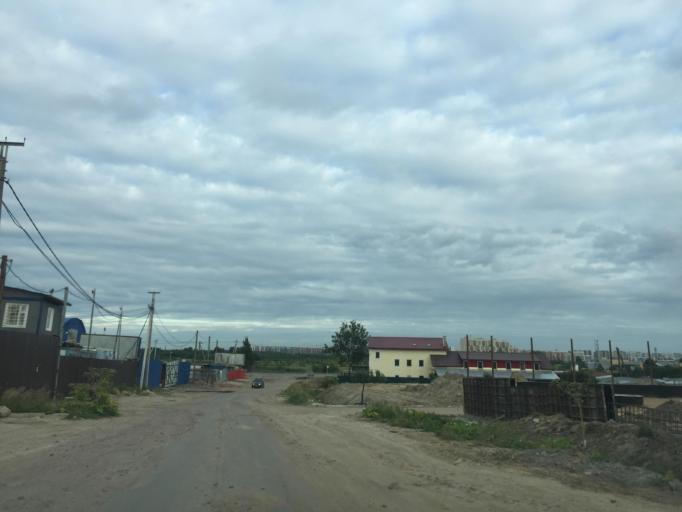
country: RU
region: Leningrad
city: Bugry
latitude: 60.0856
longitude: 30.3907
